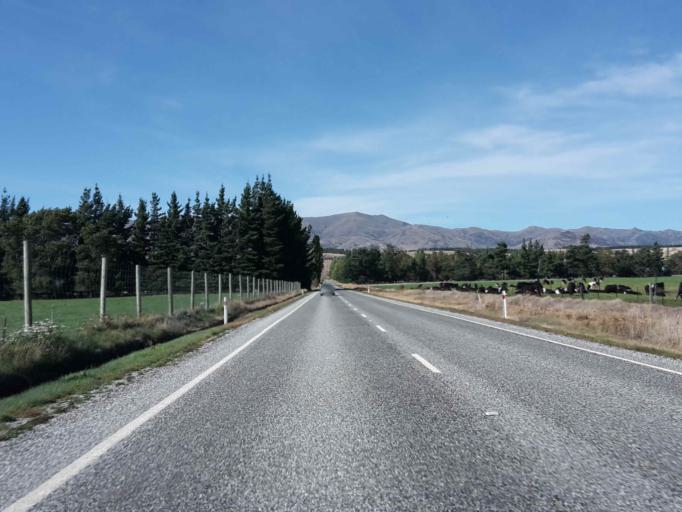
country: NZ
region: Otago
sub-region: Queenstown-Lakes District
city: Wanaka
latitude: -44.8320
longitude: 169.3766
